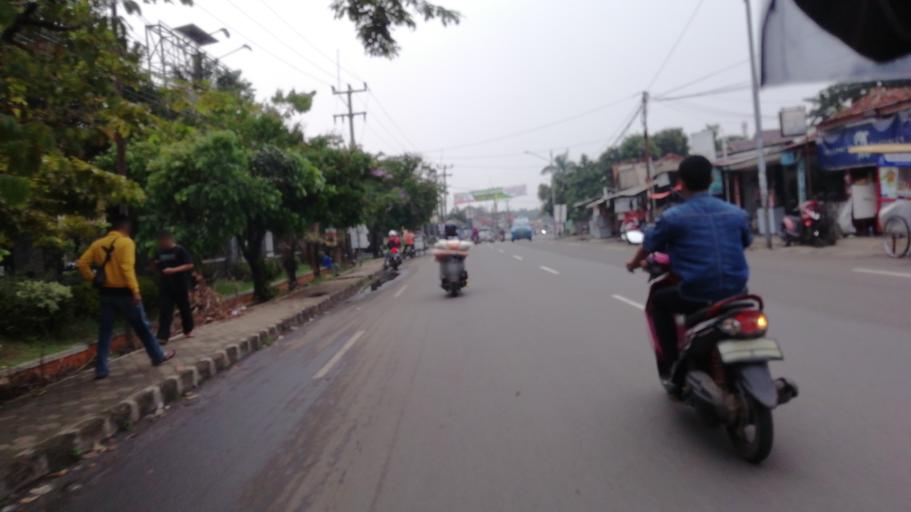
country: ID
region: West Java
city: Cibinong
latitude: -6.5224
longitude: 106.8082
